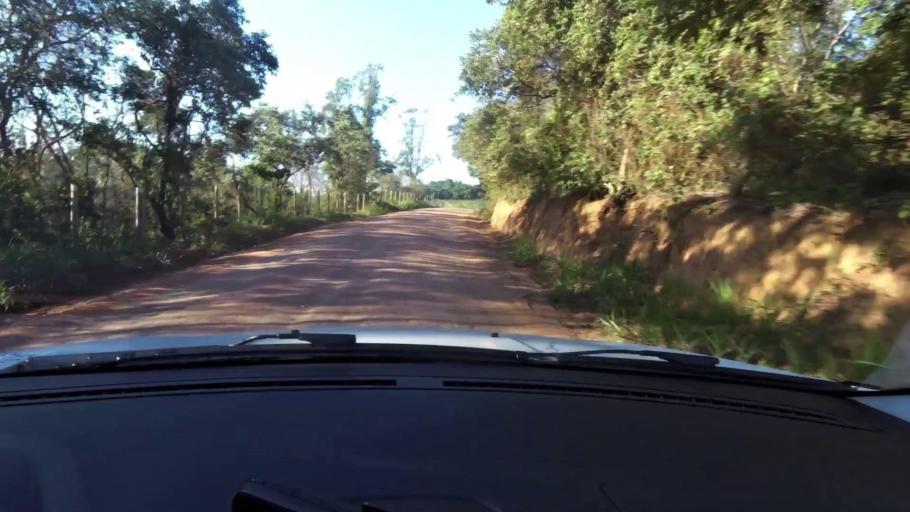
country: BR
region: Espirito Santo
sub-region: Guarapari
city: Guarapari
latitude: -20.7249
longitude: -40.5877
